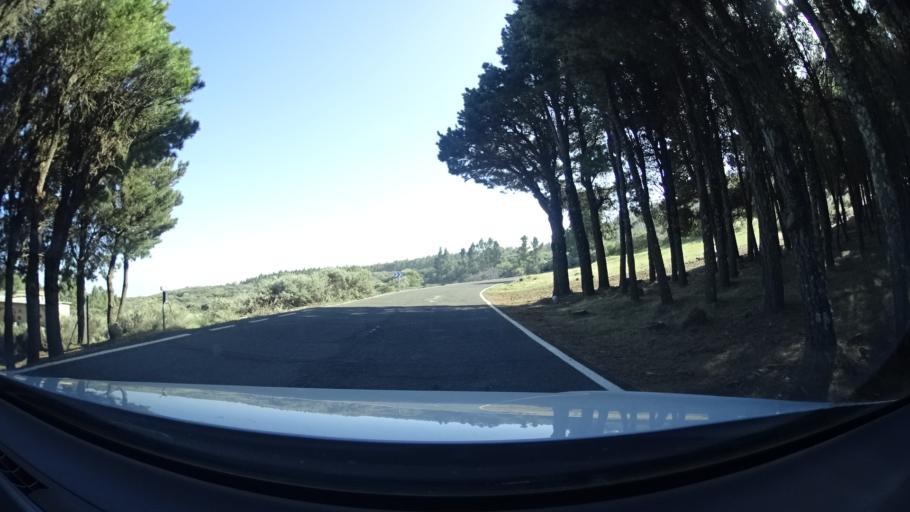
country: ES
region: Canary Islands
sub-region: Provincia de Las Palmas
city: Vega de San Mateo
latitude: 27.9645
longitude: -15.5461
